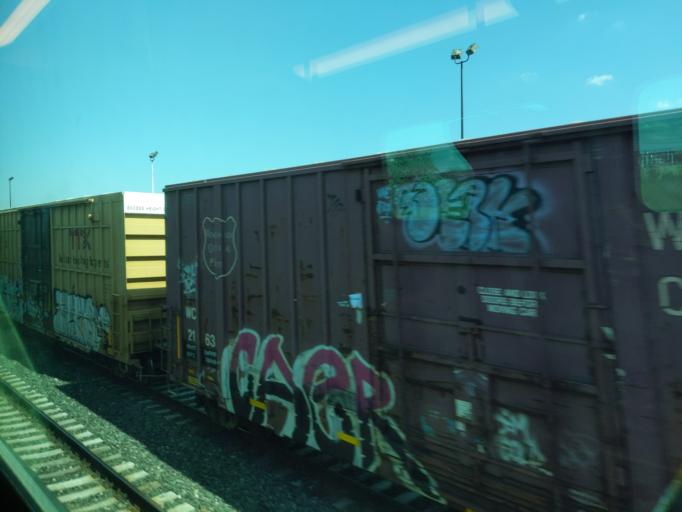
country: CA
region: Ontario
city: Etobicoke
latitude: 43.7060
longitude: -79.5844
